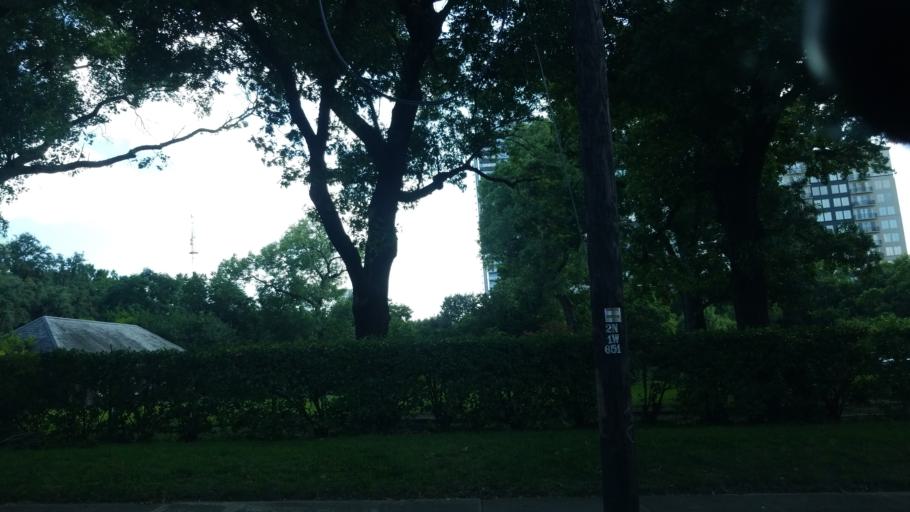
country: US
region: Texas
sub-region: Dallas County
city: Dallas
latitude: 32.7990
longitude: -96.8085
